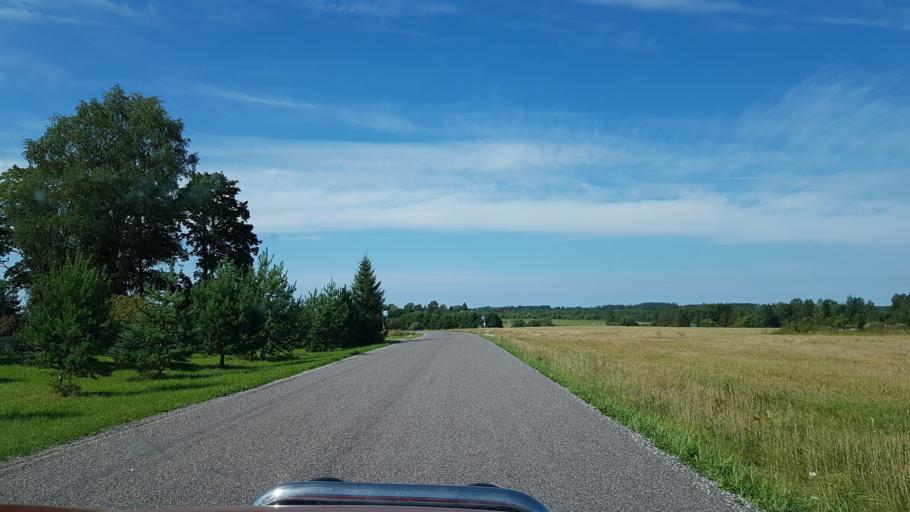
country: EE
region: Tartu
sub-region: Elva linn
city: Elva
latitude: 58.2485
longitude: 26.3620
